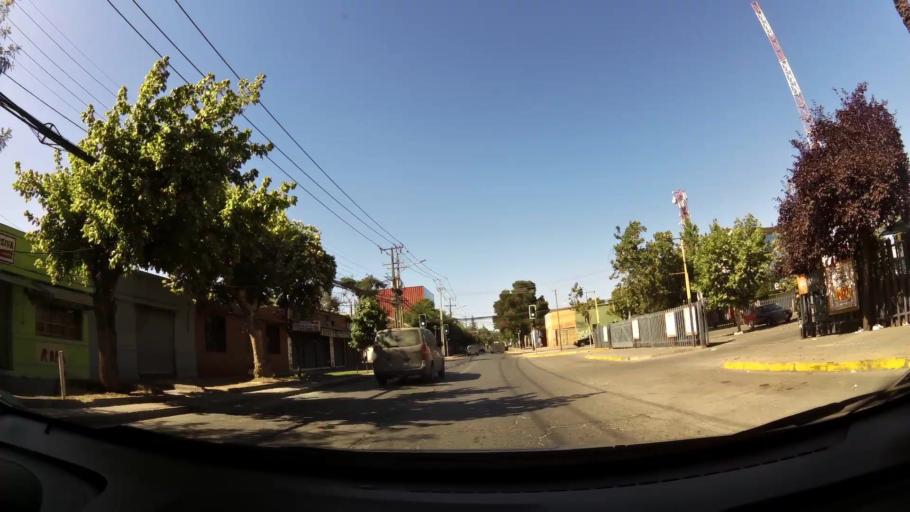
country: CL
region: O'Higgins
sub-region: Provincia de Cachapoal
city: Rancagua
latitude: -34.1699
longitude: -70.7487
